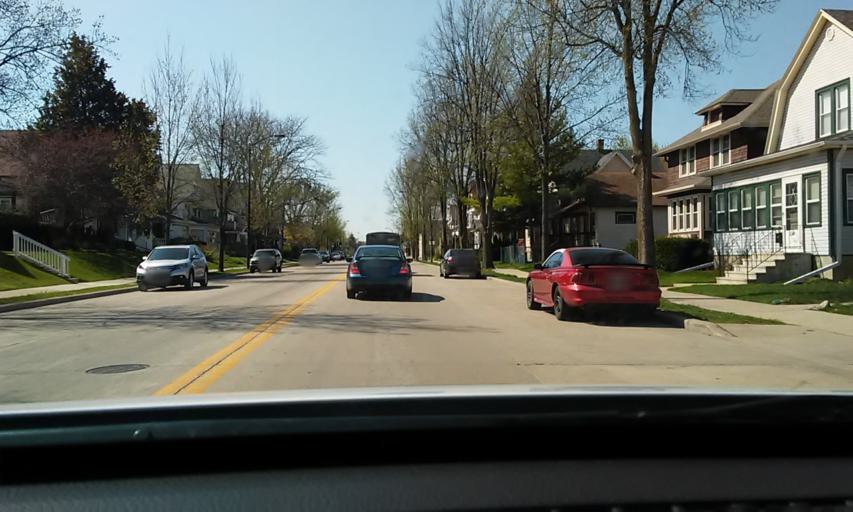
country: US
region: Wisconsin
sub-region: Milwaukee County
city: West Milwaukee
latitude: 43.0119
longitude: -87.9874
